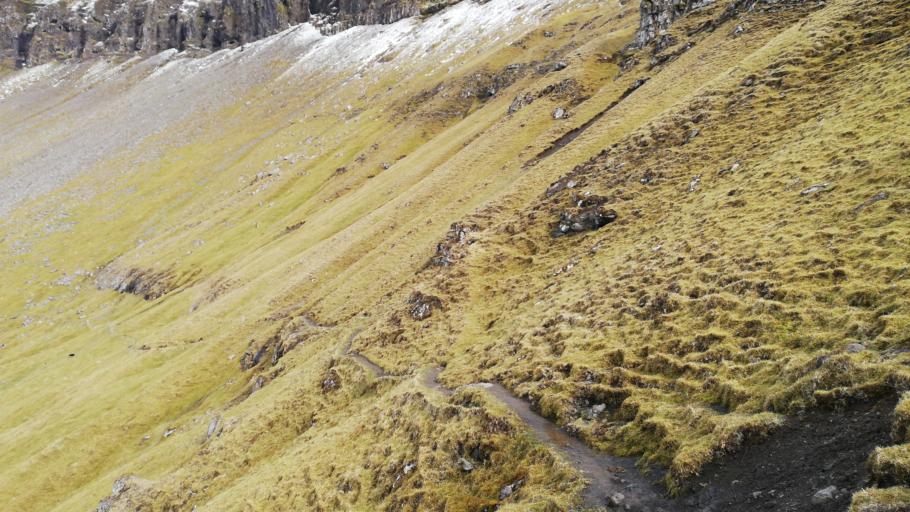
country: FO
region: Streymoy
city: Kollafjordhur
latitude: 62.0683
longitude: -6.9802
